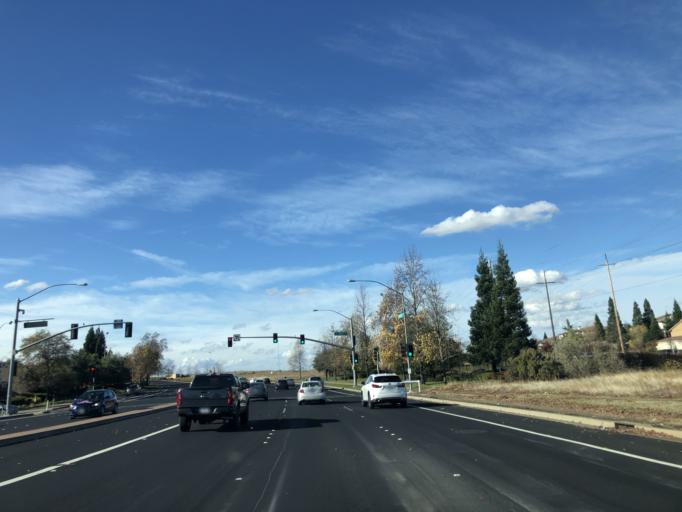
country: US
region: California
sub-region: Placer County
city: Roseville
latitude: 38.7761
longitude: -121.2781
